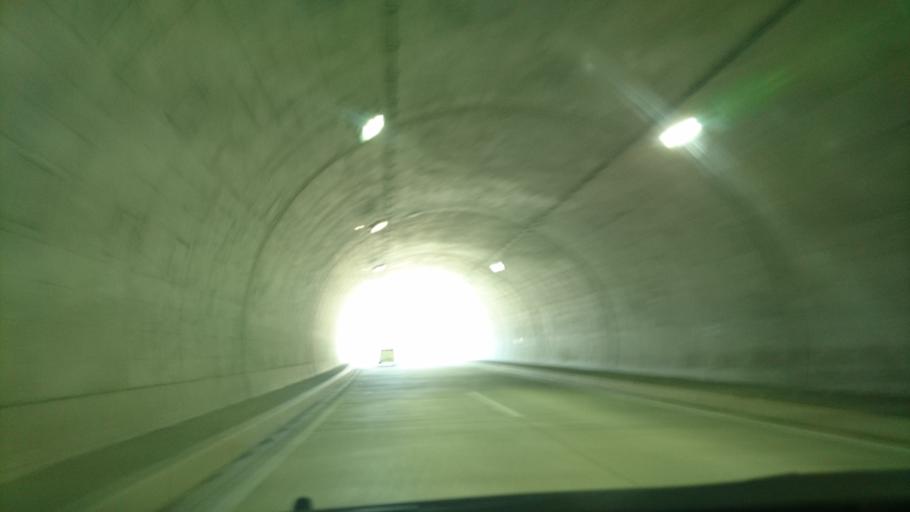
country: JP
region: Iwate
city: Ofunato
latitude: 38.8882
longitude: 141.6045
